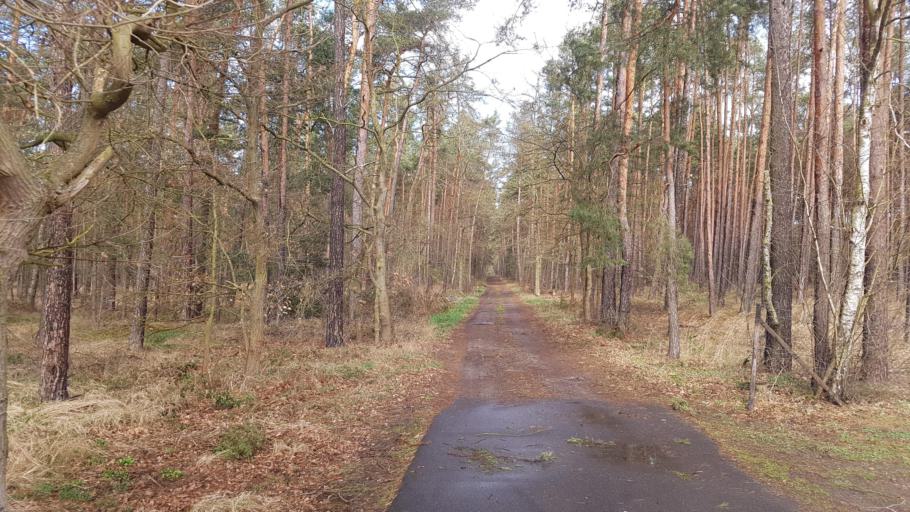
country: DE
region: Brandenburg
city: Altdobern
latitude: 51.6959
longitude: 14.0389
